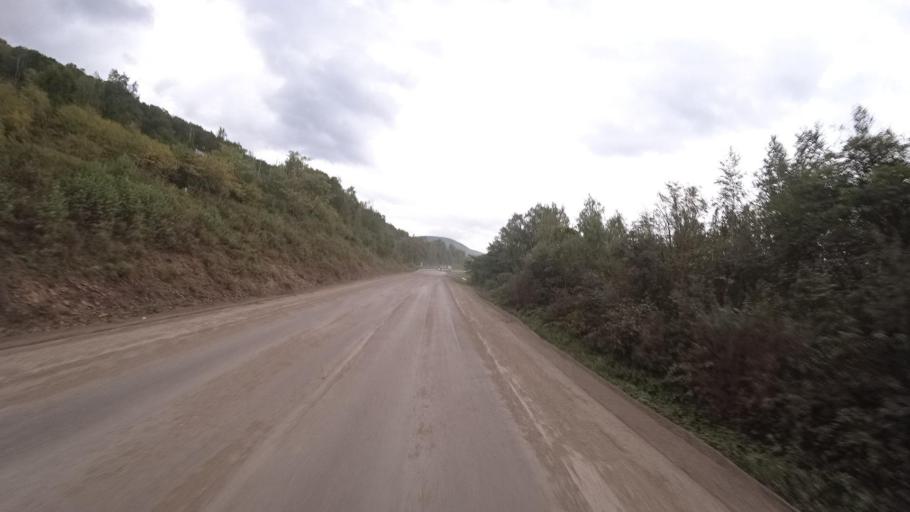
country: RU
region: Jewish Autonomous Oblast
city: Khingansk
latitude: 48.9916
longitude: 131.1113
